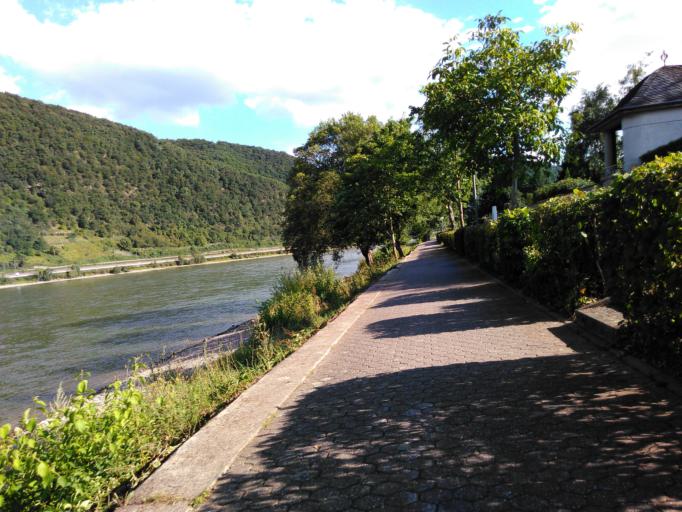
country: DE
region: Rheinland-Pfalz
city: Spay
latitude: 50.2603
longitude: 7.6496
